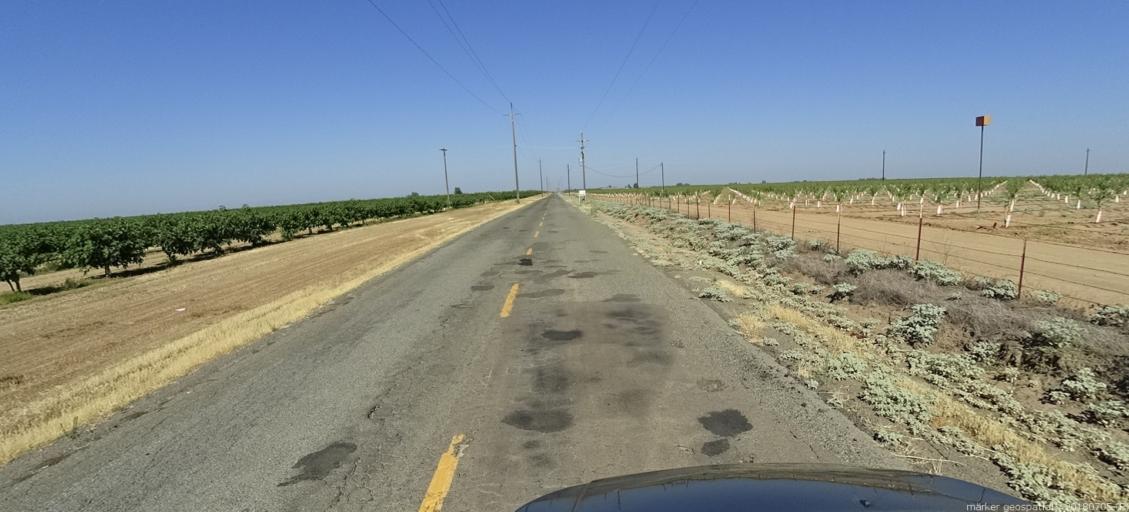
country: US
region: California
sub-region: Madera County
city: Fairmead
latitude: 37.1269
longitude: -120.0958
